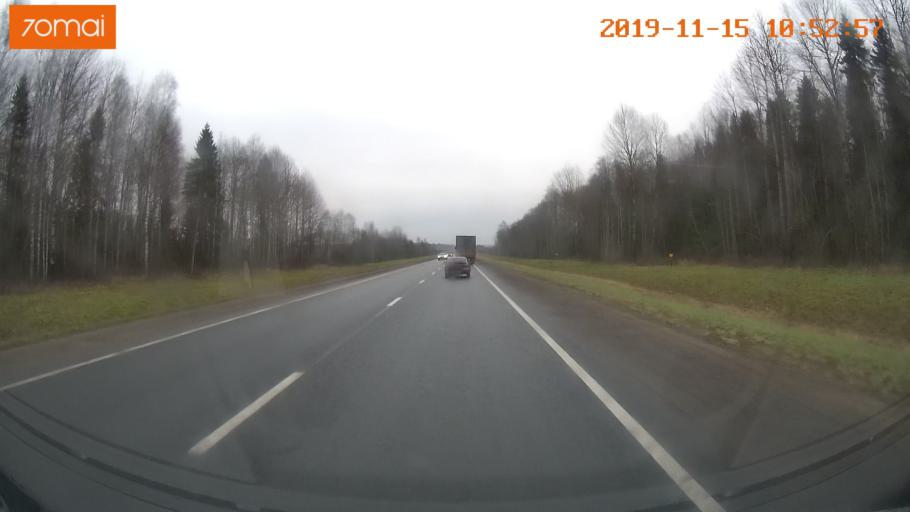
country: RU
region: Vologda
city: Chebsara
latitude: 59.1716
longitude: 38.7436
